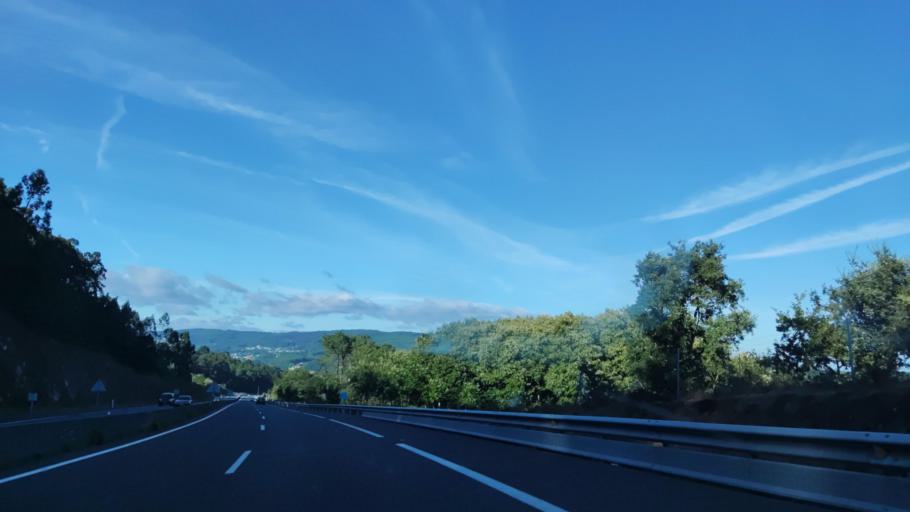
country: ES
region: Galicia
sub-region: Provincia da Coruna
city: Boiro
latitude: 42.6472
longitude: -8.9039
